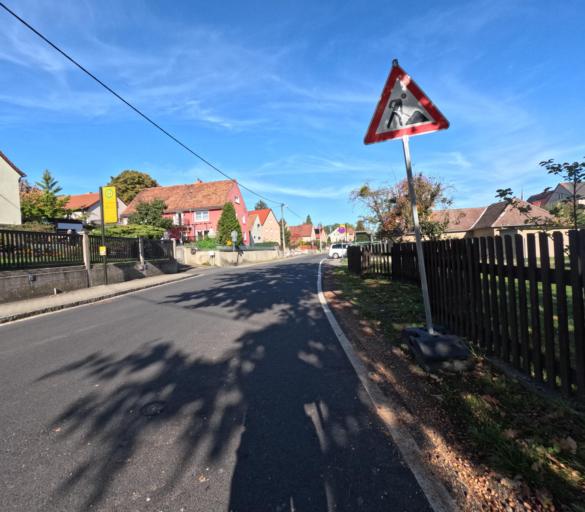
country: DE
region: Saxony
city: Ottendorf-Okrilla
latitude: 51.1301
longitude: 13.8400
